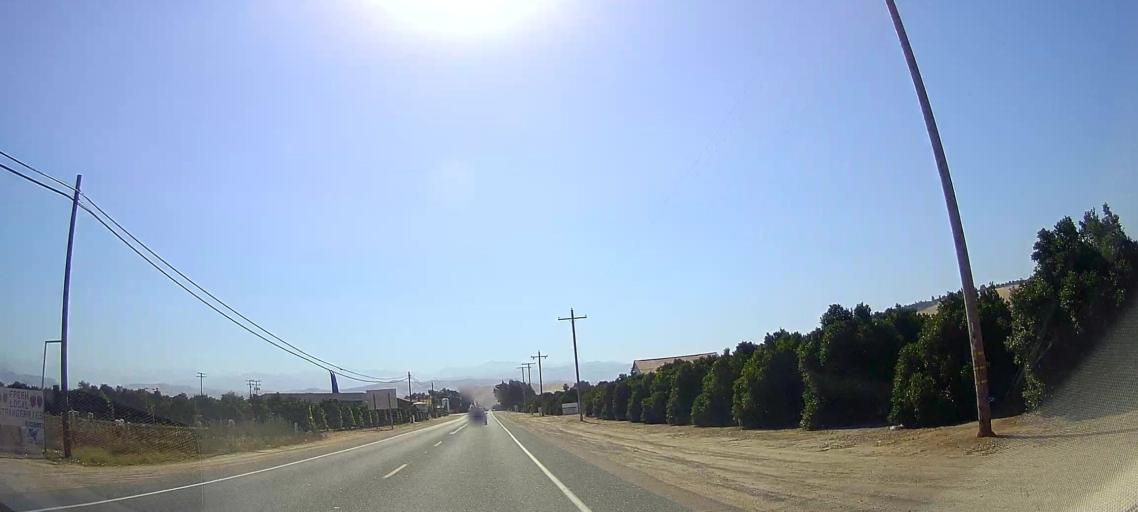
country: US
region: California
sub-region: Tulare County
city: Exeter
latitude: 36.3260
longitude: -119.1102
